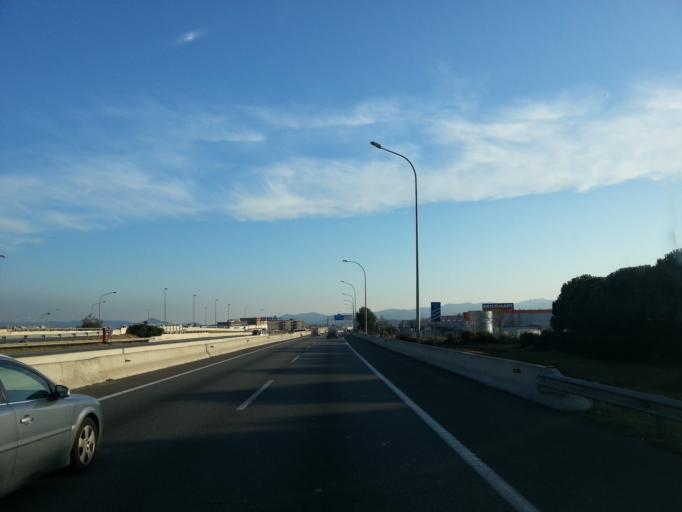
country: ES
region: Catalonia
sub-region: Provincia de Barcelona
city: Sant Quirze del Valles
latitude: 41.5335
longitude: 2.0903
